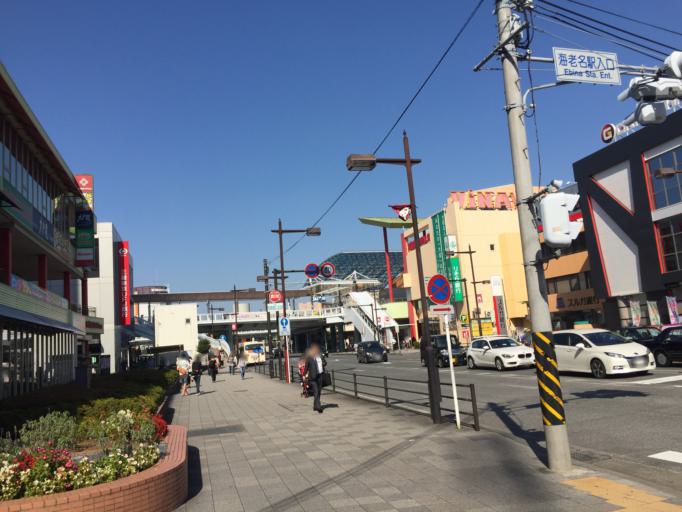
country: JP
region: Kanagawa
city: Atsugi
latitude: 35.4515
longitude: 139.3923
